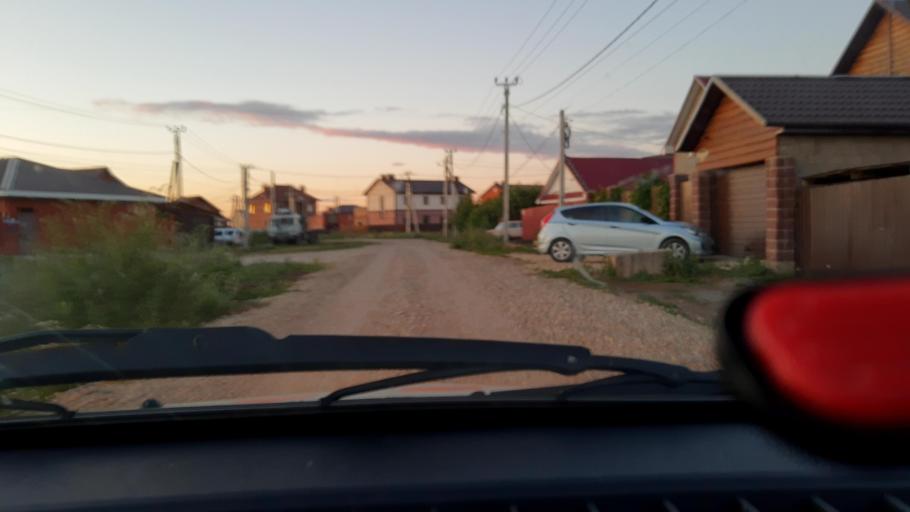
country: RU
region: Bashkortostan
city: Ufa
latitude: 54.6317
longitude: 55.9128
